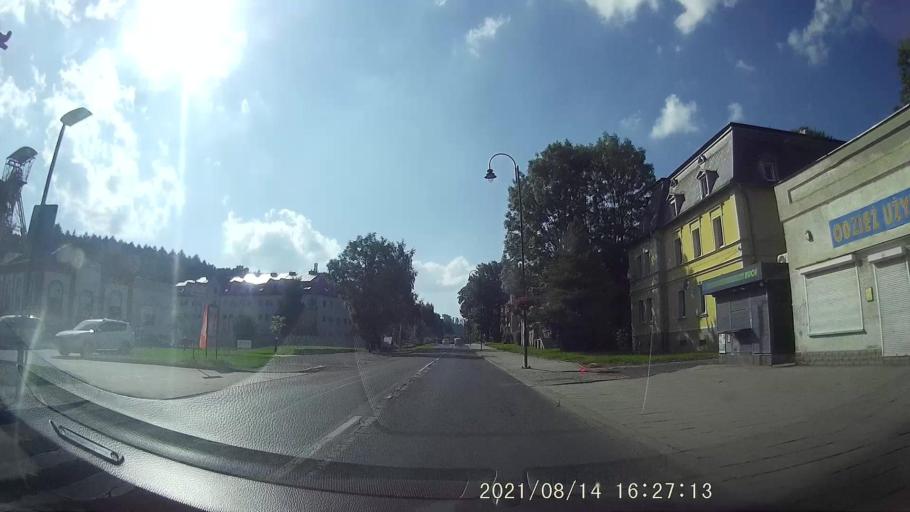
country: PL
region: Lower Silesian Voivodeship
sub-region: Powiat walbrzyski
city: Czarny Bor
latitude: 50.7645
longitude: 16.1665
